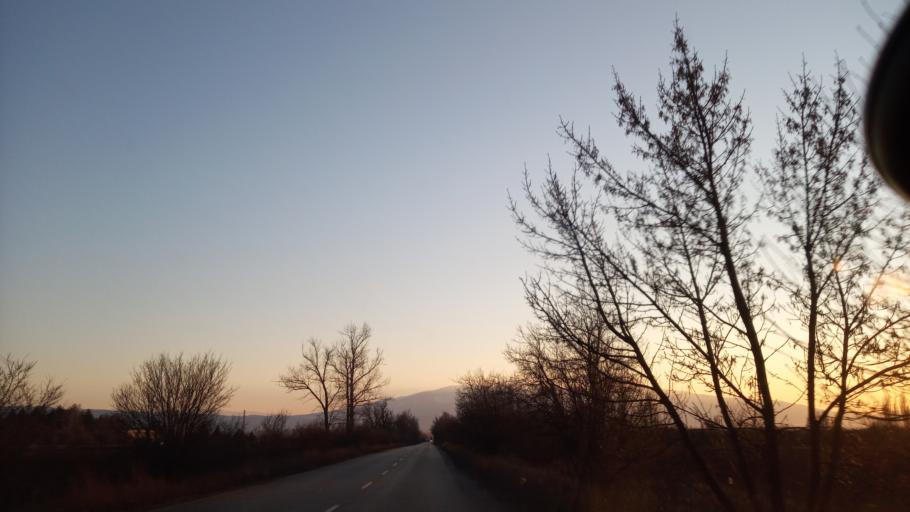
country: BG
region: Sofia-Capital
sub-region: Stolichna Obshtina
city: Bukhovo
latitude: 42.7462
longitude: 23.4765
